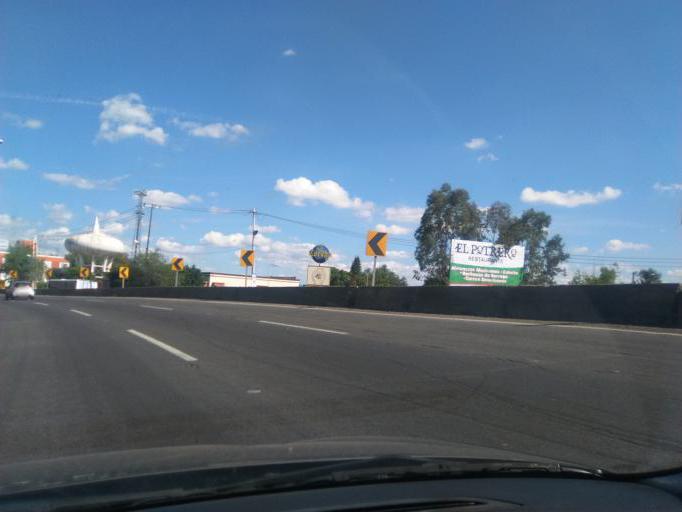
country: MX
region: Guanajuato
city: Silao
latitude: 20.9548
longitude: -101.4392
